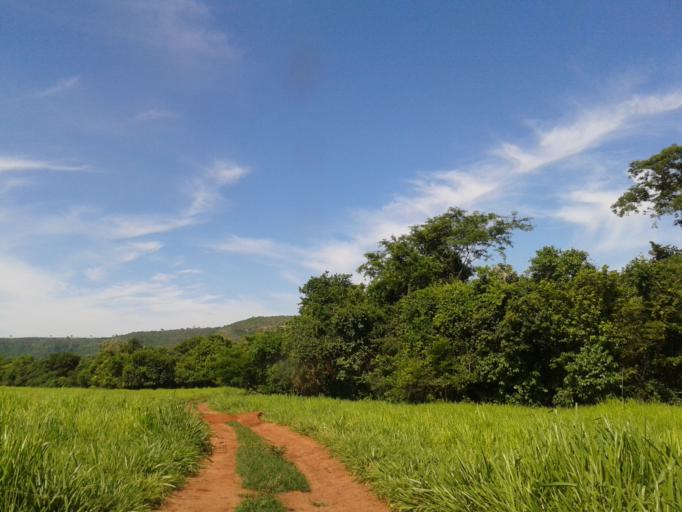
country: BR
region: Minas Gerais
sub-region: Santa Vitoria
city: Santa Vitoria
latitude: -19.0816
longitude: -50.0182
